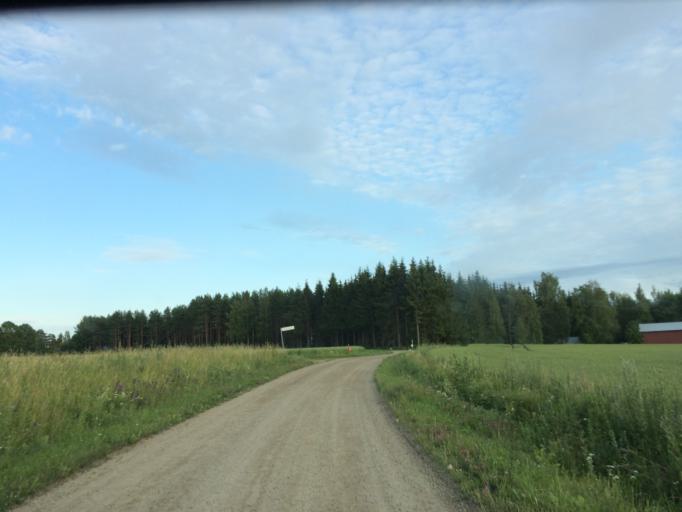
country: FI
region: Haeme
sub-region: Haemeenlinna
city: Janakkala
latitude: 60.8782
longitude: 24.6170
